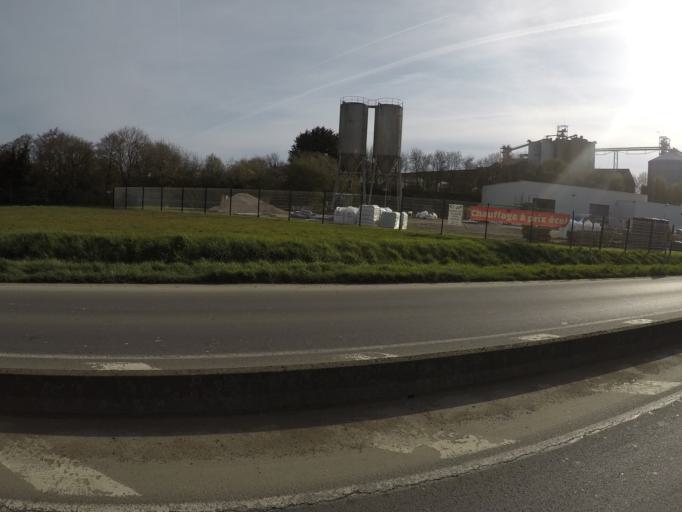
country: FR
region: Brittany
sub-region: Departement des Cotes-d'Armor
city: Plouagat
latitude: 48.5313
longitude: -2.9703
